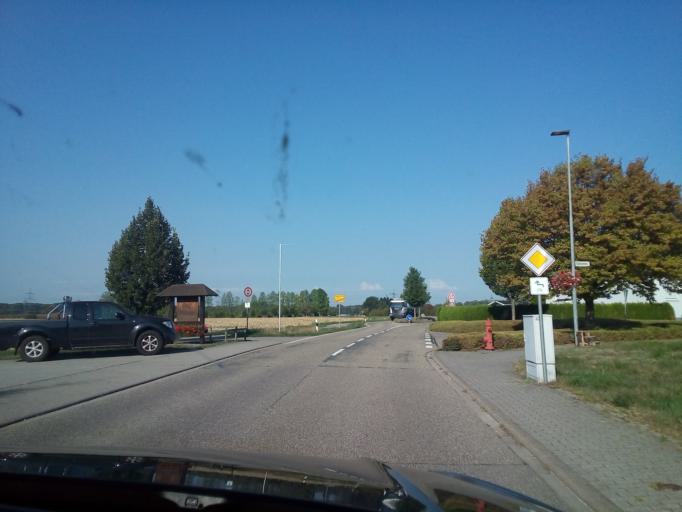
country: DE
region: Baden-Wuerttemberg
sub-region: Karlsruhe Region
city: Sinzheim
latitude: 48.7718
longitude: 8.1605
